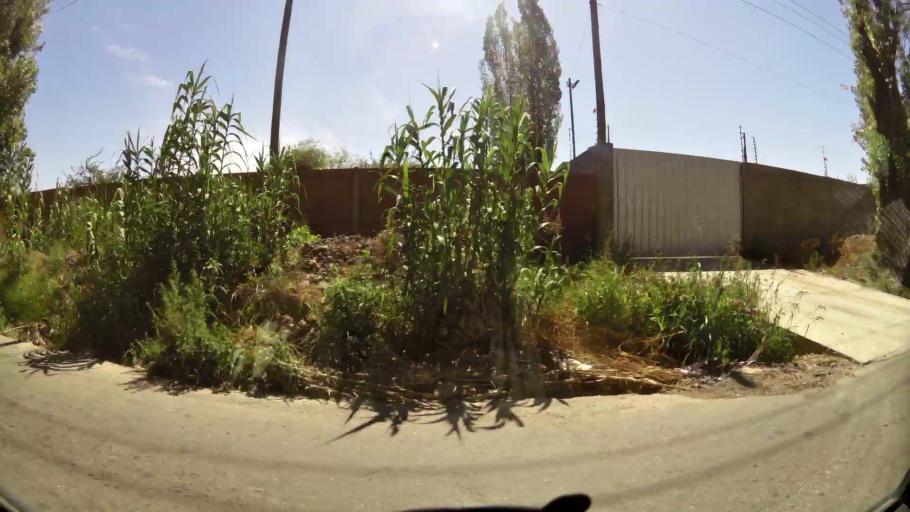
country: AR
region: Mendoza
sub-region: Departamento de Godoy Cruz
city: Godoy Cruz
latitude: -32.9760
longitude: -68.8401
